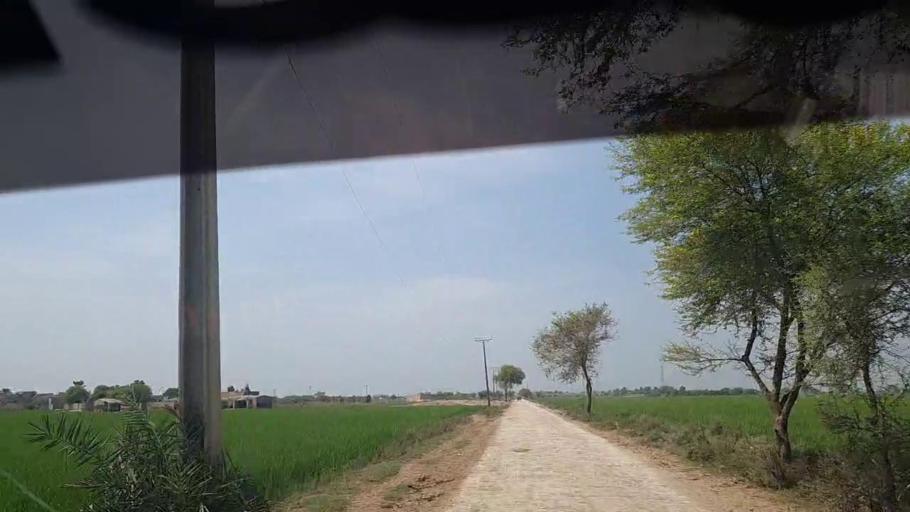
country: PK
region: Sindh
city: Thul
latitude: 28.1745
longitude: 68.7420
